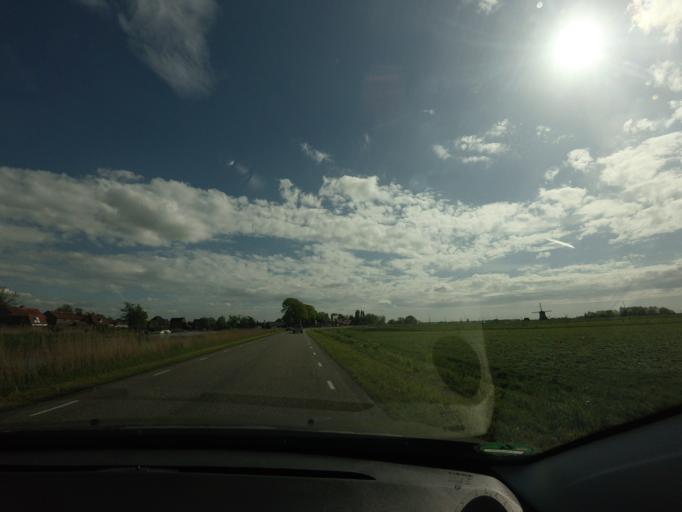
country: NL
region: North Holland
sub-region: Gemeente Heerhugowaard
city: Heerhugowaard
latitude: 52.6369
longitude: 4.8763
